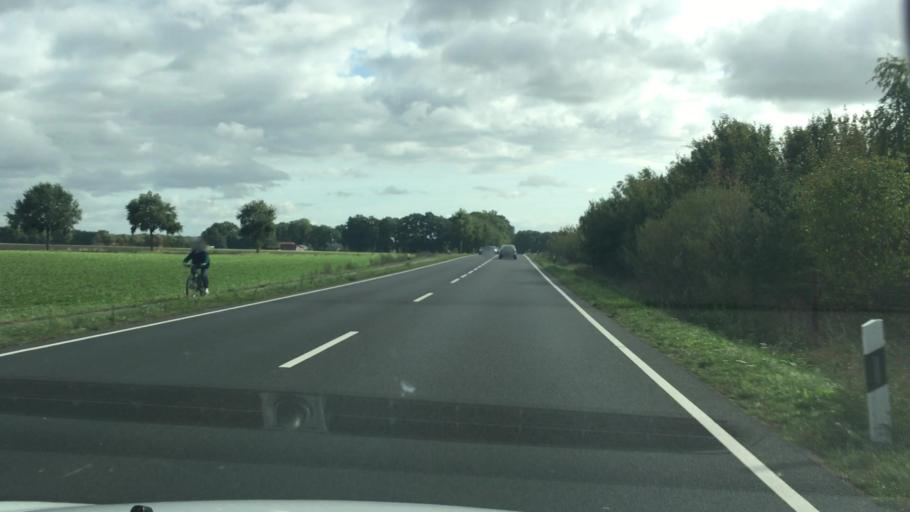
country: DE
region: Lower Saxony
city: Diepholz
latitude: 52.6420
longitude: 8.3464
